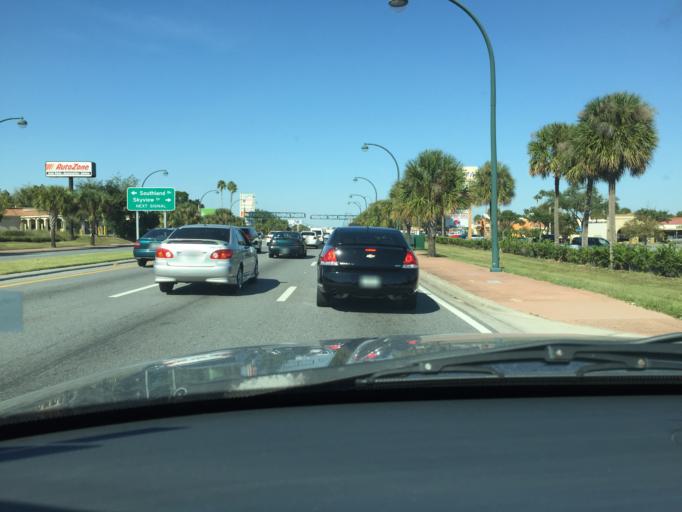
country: US
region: Florida
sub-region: Orange County
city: Sky Lake
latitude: 28.4542
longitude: -81.3996
